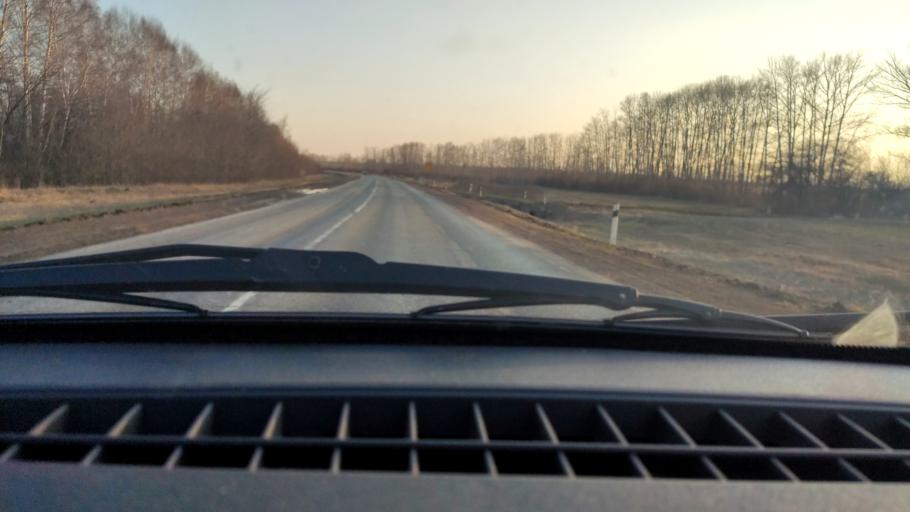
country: RU
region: Bashkortostan
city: Davlekanovo
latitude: 54.3517
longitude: 55.1808
